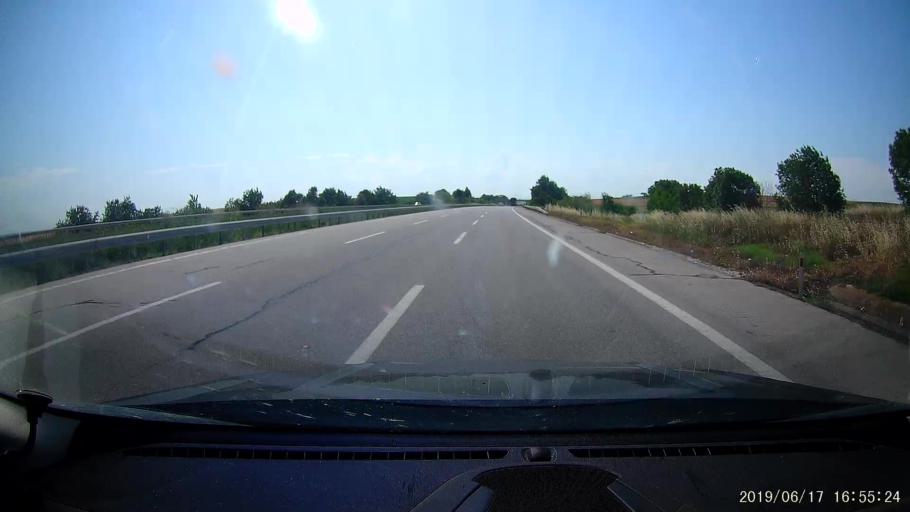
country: TR
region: Edirne
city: Haskoy
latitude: 41.5786
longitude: 26.9663
